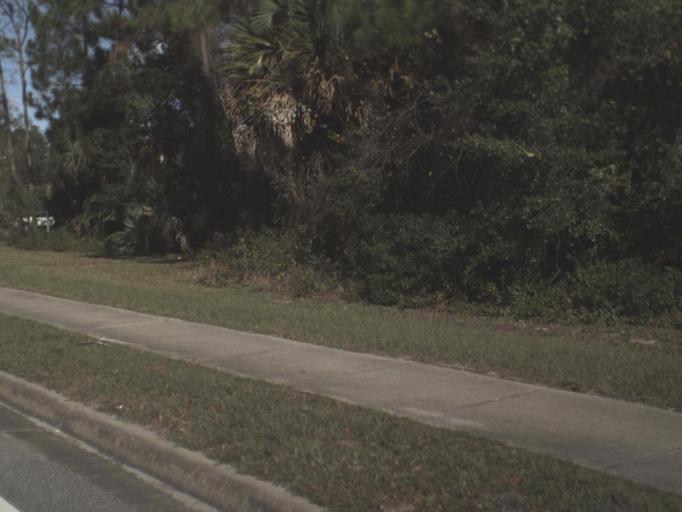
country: US
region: Florida
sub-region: Volusia County
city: South Daytona
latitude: 29.1423
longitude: -81.0352
